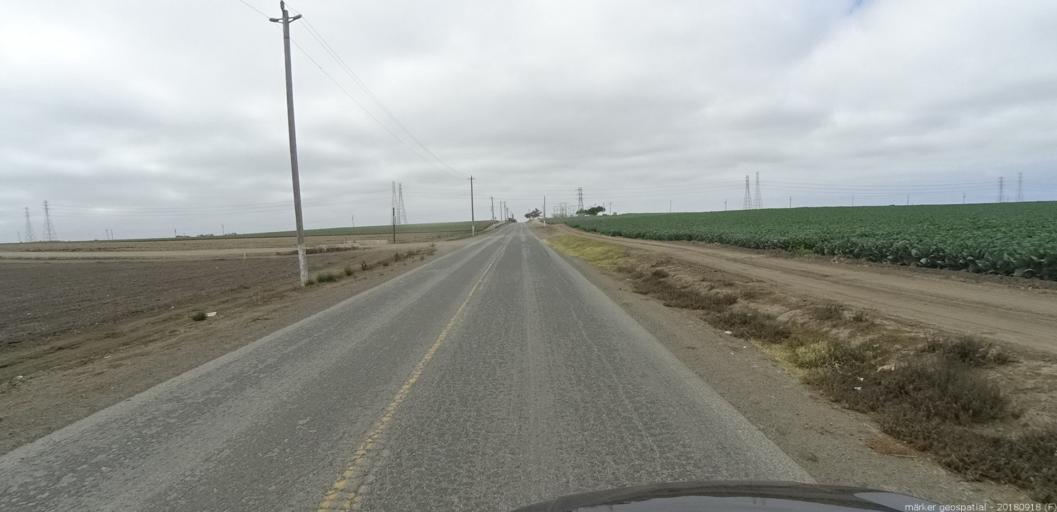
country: US
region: California
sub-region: Monterey County
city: Castroville
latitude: 36.7644
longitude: -121.7298
